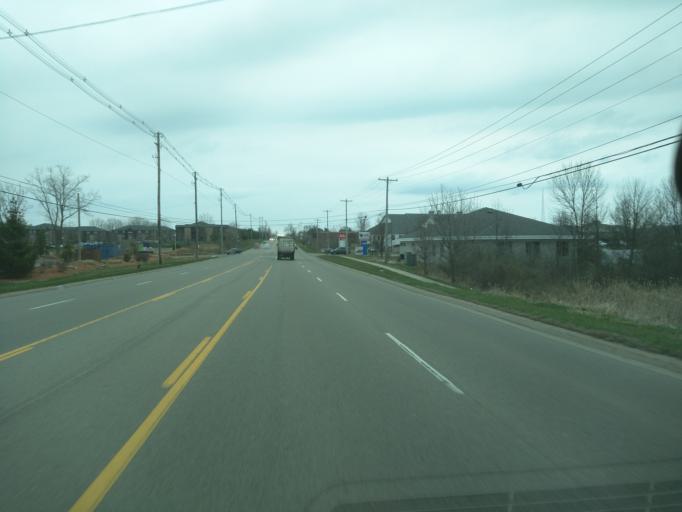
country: US
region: Michigan
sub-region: Ingham County
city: Holt
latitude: 42.6829
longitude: -84.5101
